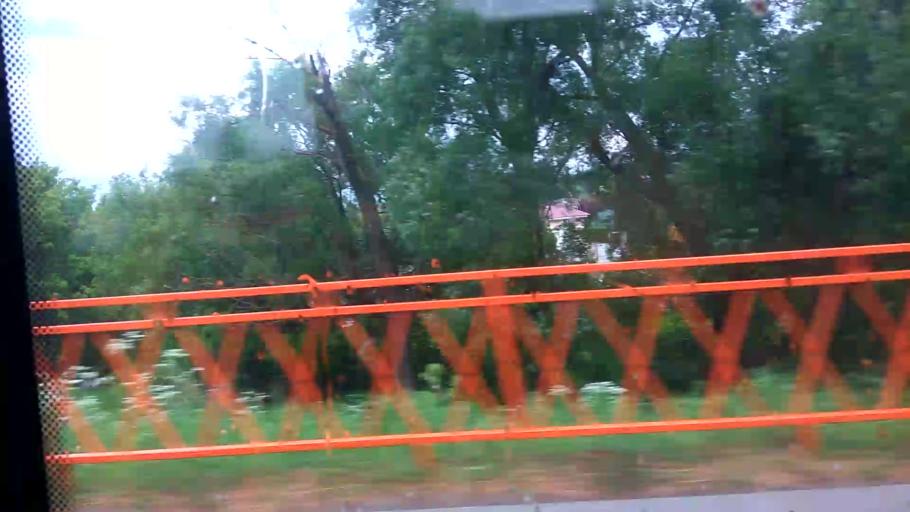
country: RU
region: Moskovskaya
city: Zaraysk
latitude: 54.7552
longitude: 38.8623
